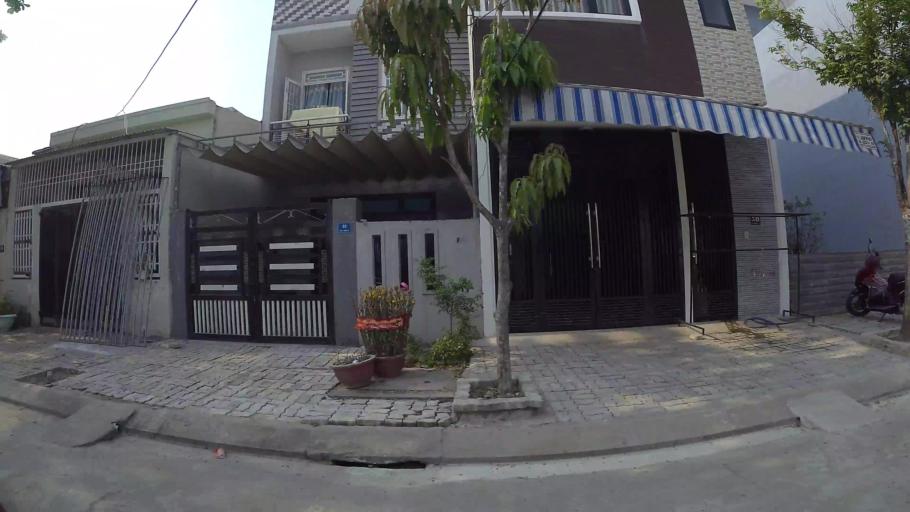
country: VN
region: Da Nang
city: Lien Chieu
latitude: 16.0518
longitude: 108.1667
